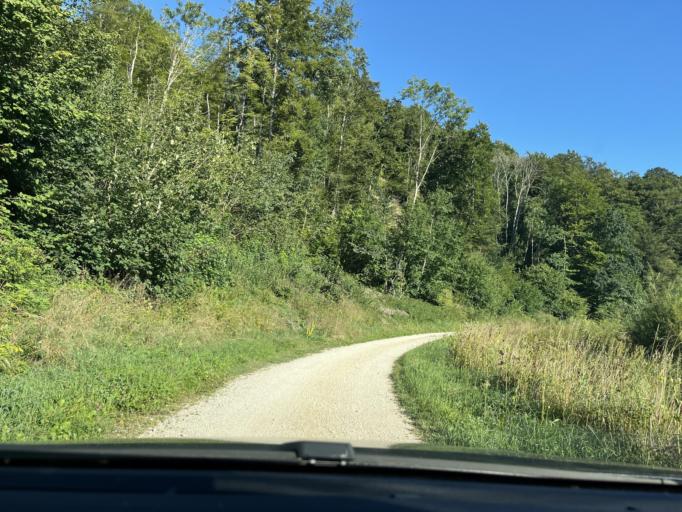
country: DE
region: Baden-Wuerttemberg
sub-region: Tuebingen Region
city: Veringenstadt
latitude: 48.1912
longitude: 9.2158
